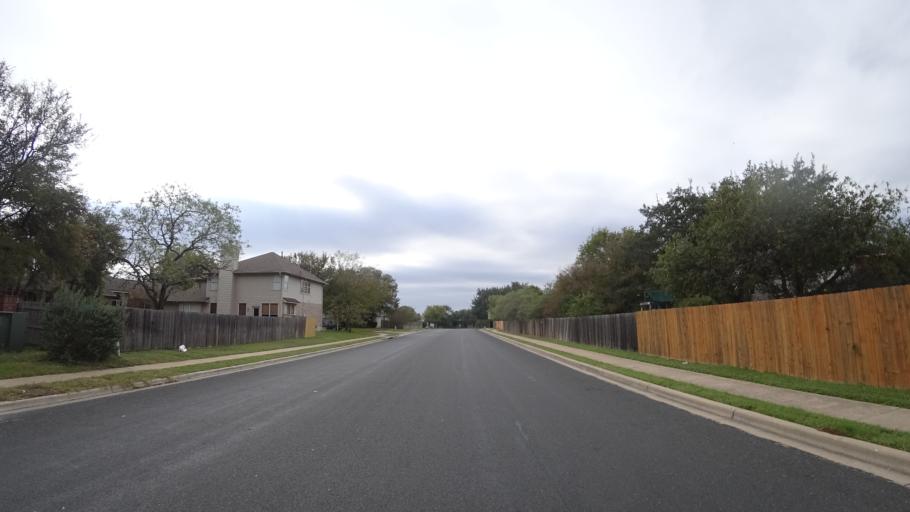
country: US
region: Texas
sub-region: Travis County
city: Shady Hollow
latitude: 30.1560
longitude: -97.8519
